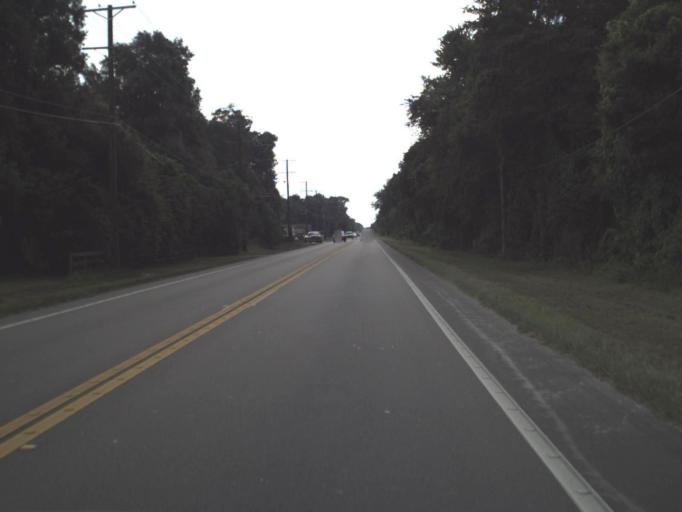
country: US
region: Florida
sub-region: Hillsborough County
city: Plant City
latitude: 28.0216
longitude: -82.0881
